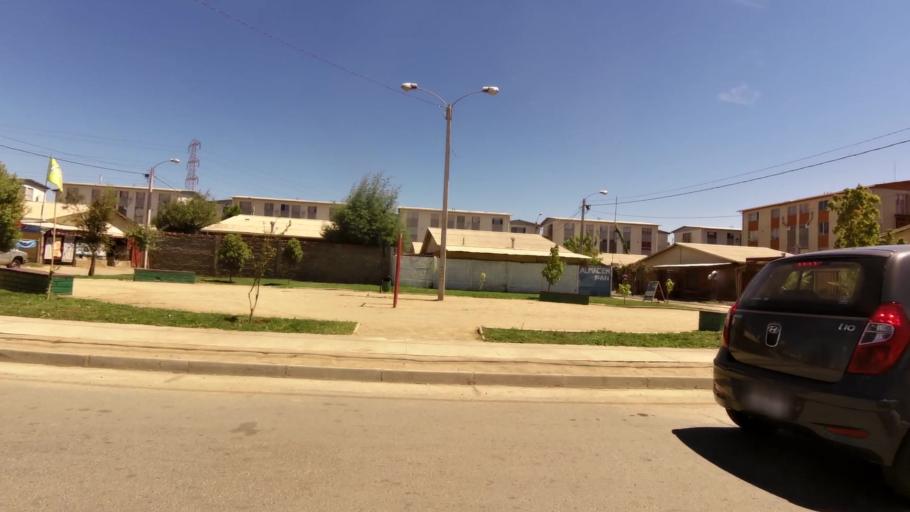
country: CL
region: O'Higgins
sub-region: Provincia de Cachapoal
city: Rancagua
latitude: -34.1469
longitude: -70.7232
